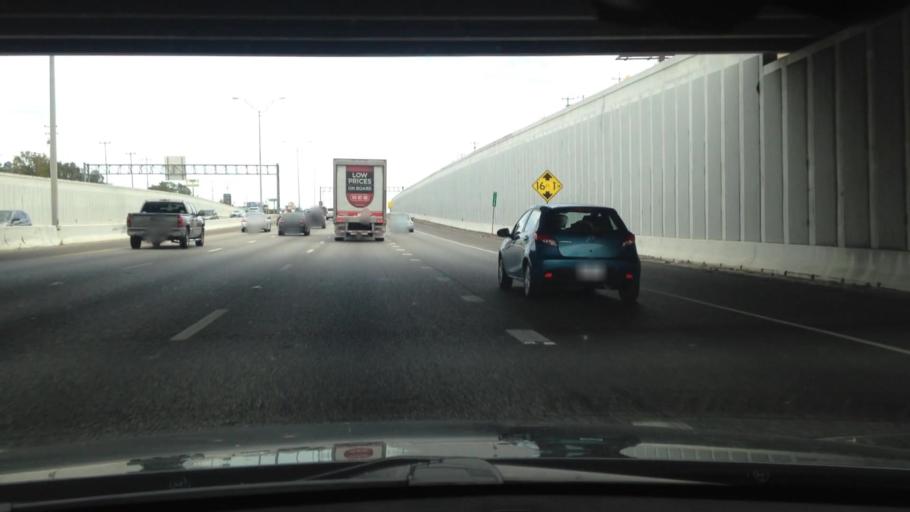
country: US
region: Texas
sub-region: Bexar County
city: Selma
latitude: 29.5928
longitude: -98.2897
